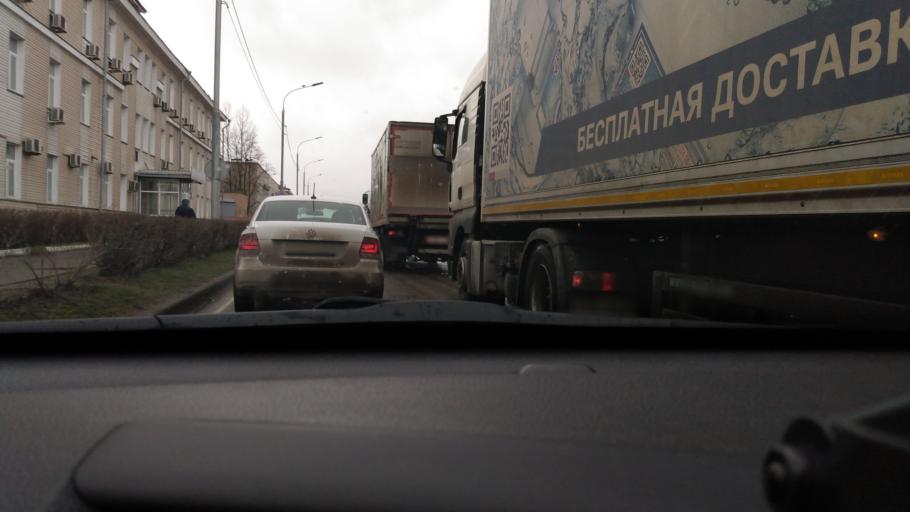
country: RU
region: Moskovskaya
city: Lobnya
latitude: 55.9838
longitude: 37.4102
